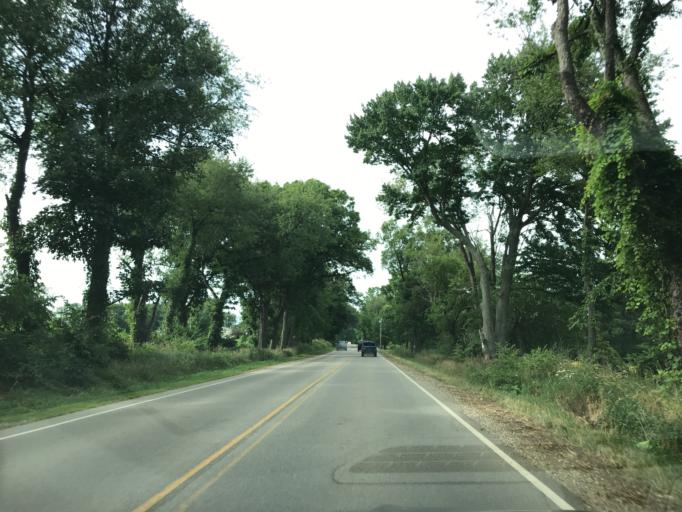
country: US
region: Michigan
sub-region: Jackson County
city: Spring Arbor
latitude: 42.0690
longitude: -84.5166
